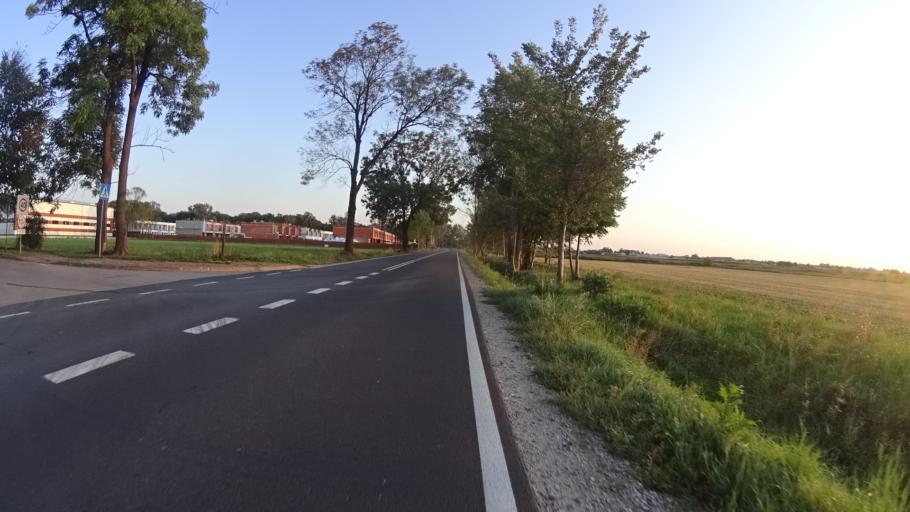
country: PL
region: Masovian Voivodeship
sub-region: Powiat warszawski zachodni
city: Ozarow Mazowiecki
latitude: 52.2217
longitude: 20.7737
